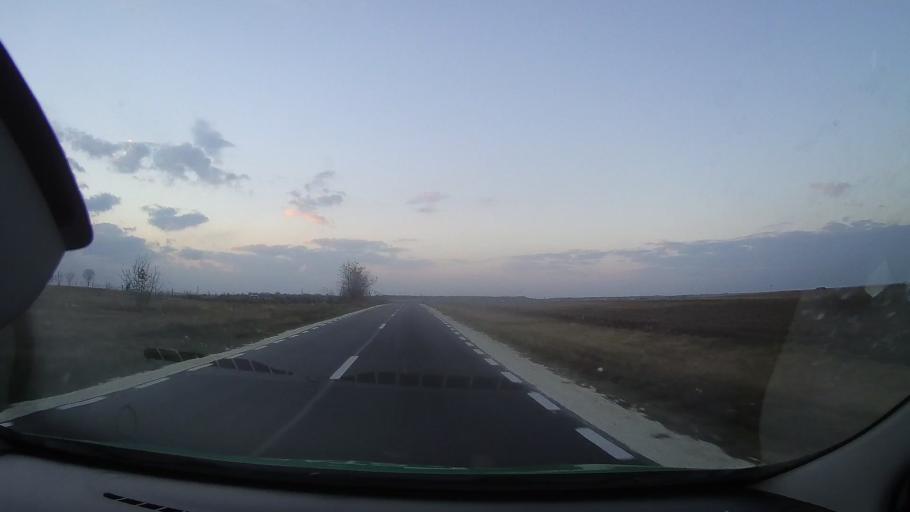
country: RO
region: Constanta
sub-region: Comuna Baneasa
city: Baneasa
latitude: 44.0951
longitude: 27.6841
